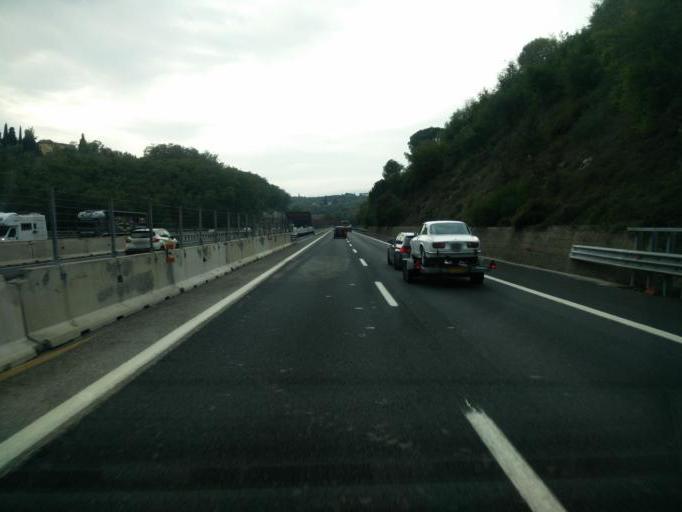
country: IT
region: Tuscany
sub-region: Province of Florence
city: Tavarnuzze
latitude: 43.7269
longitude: 11.2136
